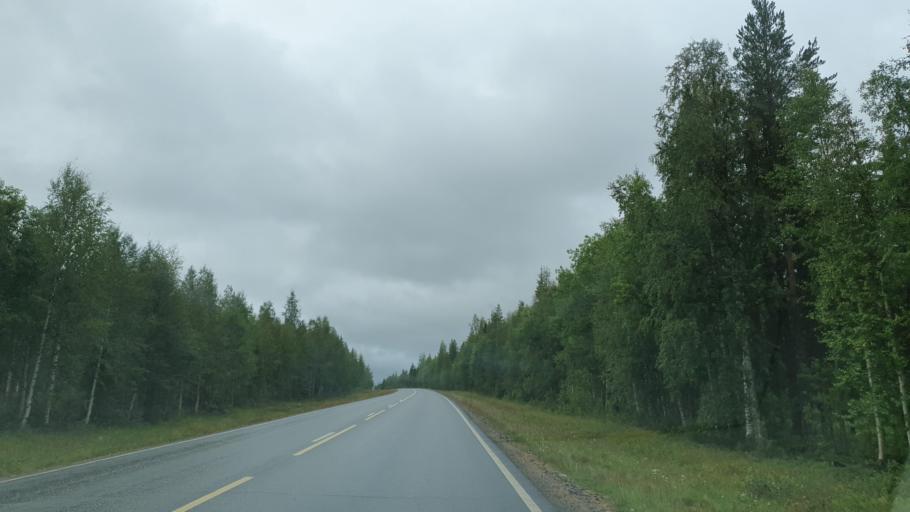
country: FI
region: Lapland
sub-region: Tunturi-Lappi
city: Kolari
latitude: 67.4090
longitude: 23.8006
